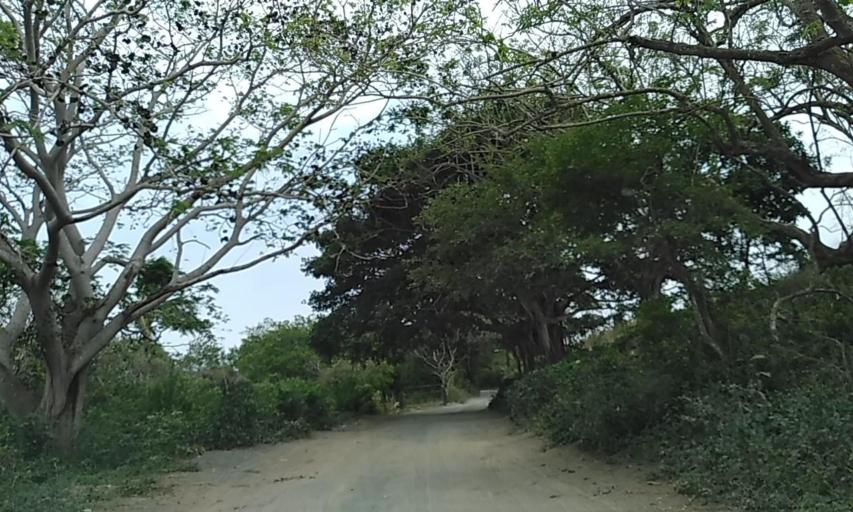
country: MX
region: Veracruz
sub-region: La Antigua
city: Nicolas Blanco (San Pancho)
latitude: 19.3113
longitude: -96.3060
